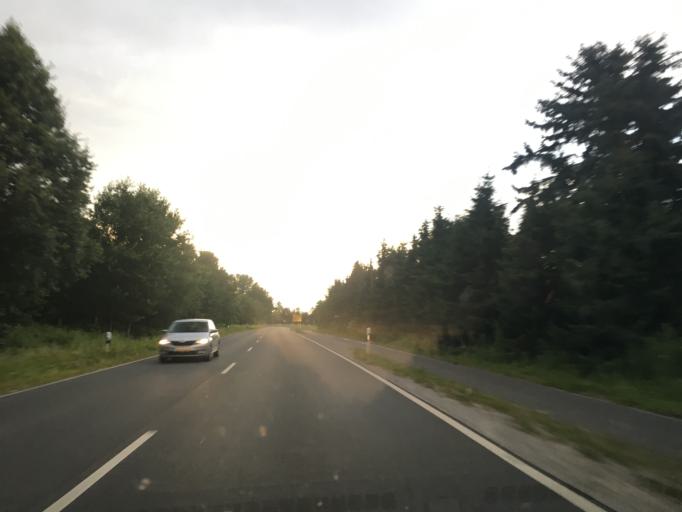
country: DE
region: North Rhine-Westphalia
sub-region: Regierungsbezirk Munster
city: Telgte
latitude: 51.9352
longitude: 7.7154
